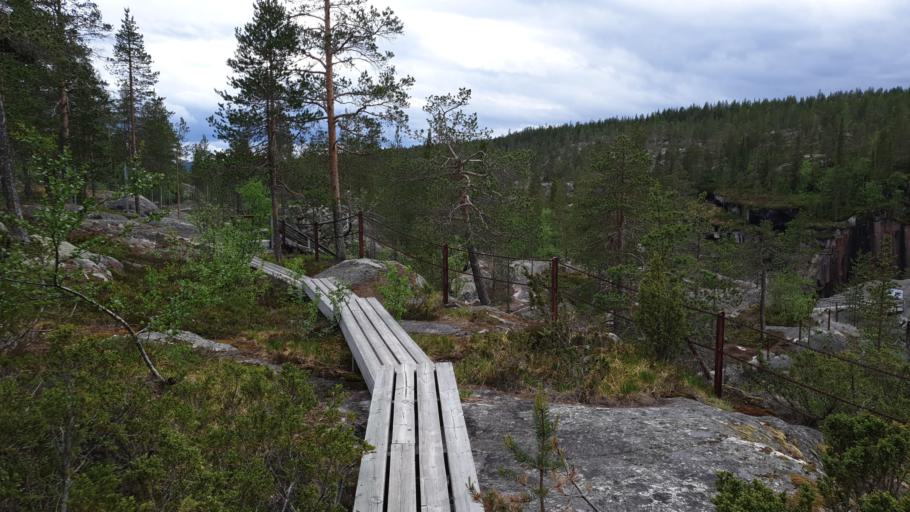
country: SE
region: Norrbotten
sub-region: Jokkmokks Kommun
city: Jokkmokk
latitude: 66.8780
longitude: 19.8190
